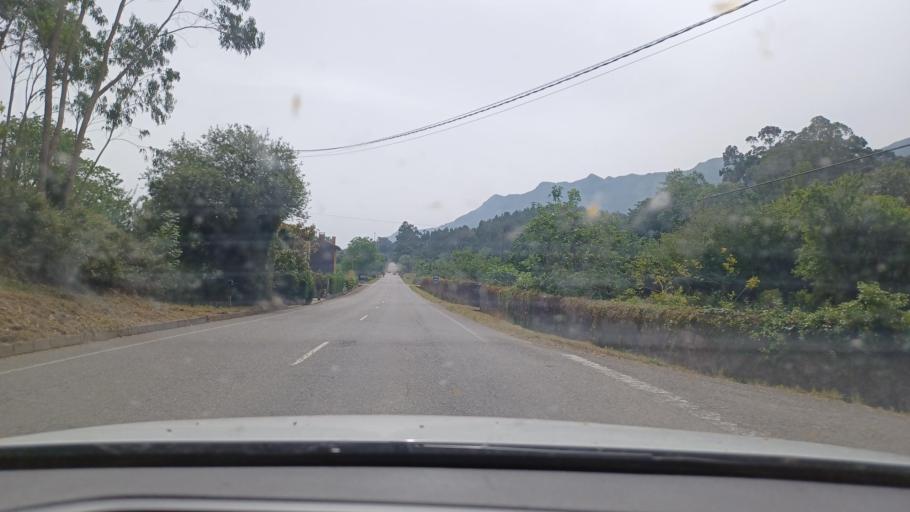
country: ES
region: Asturias
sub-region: Province of Asturias
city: Ribadesella
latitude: 43.4470
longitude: -5.0154
